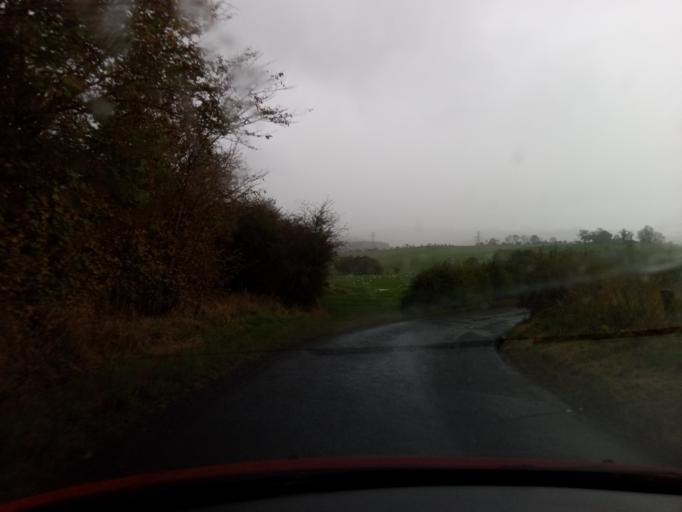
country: GB
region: Scotland
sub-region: The Scottish Borders
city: Selkirk
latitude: 55.5077
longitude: -2.7931
